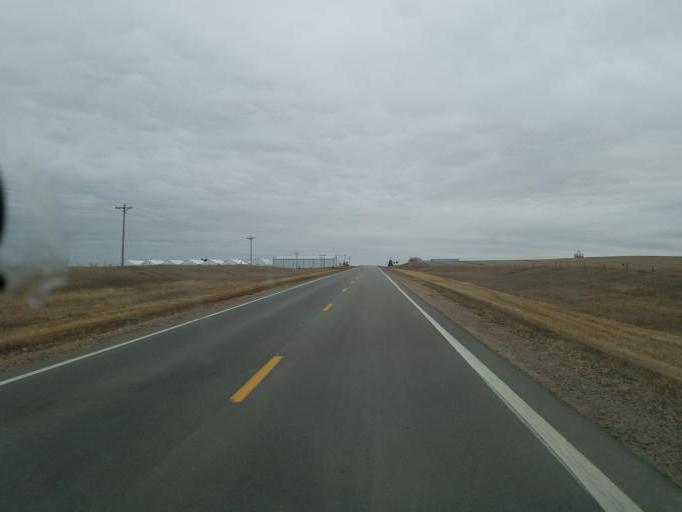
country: US
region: Nebraska
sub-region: Cedar County
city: Hartington
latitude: 42.6126
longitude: -97.2888
